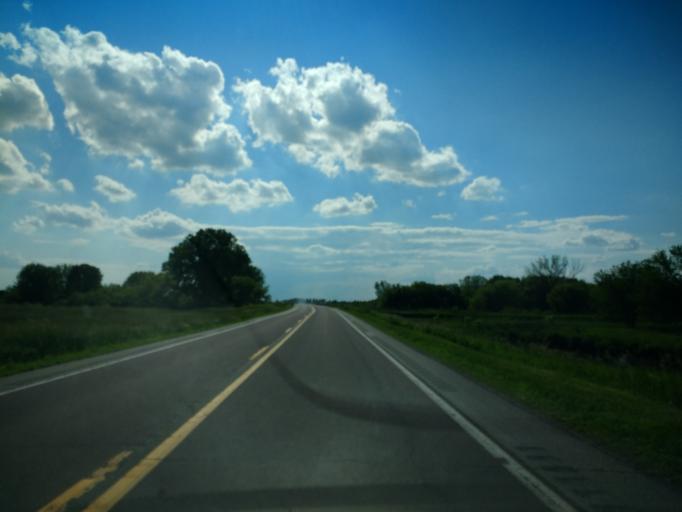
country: US
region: Iowa
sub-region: Clay County
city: Spencer
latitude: 43.1843
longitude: -95.1889
